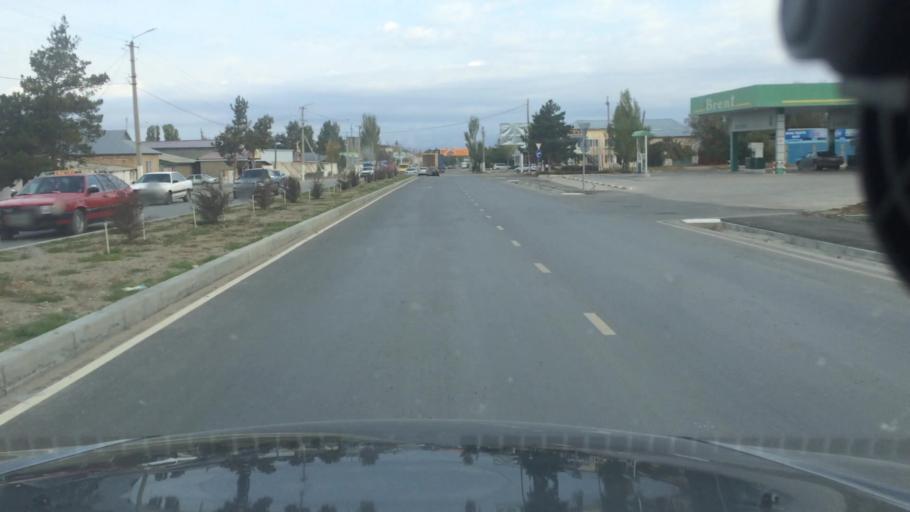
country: KG
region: Ysyk-Koel
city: Karakol
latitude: 42.5102
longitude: 78.3857
